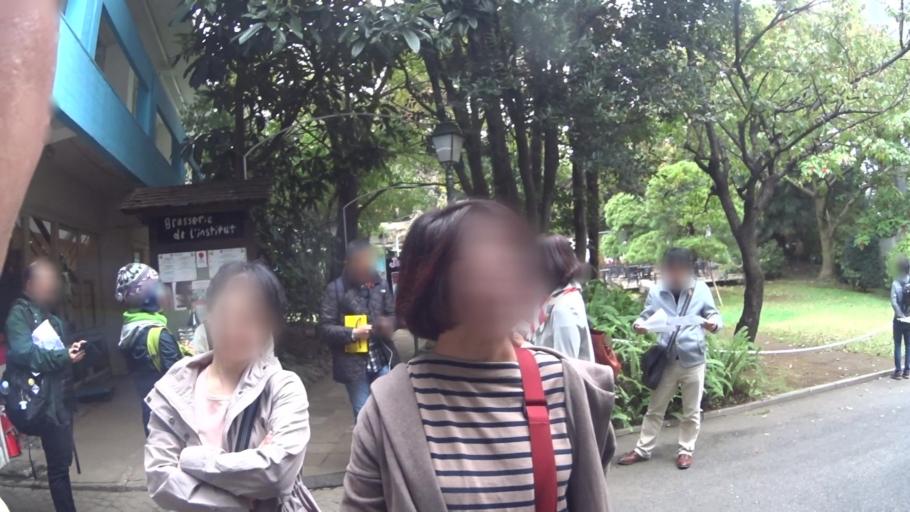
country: JP
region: Tokyo
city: Tokyo
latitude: 35.6983
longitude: 139.7400
